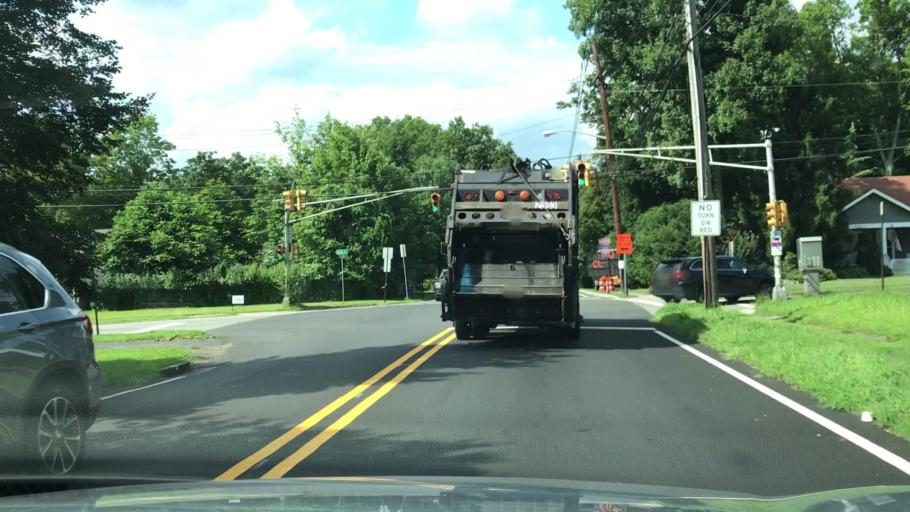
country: US
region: New Jersey
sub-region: Bergen County
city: Closter
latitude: 40.9688
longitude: -73.9739
